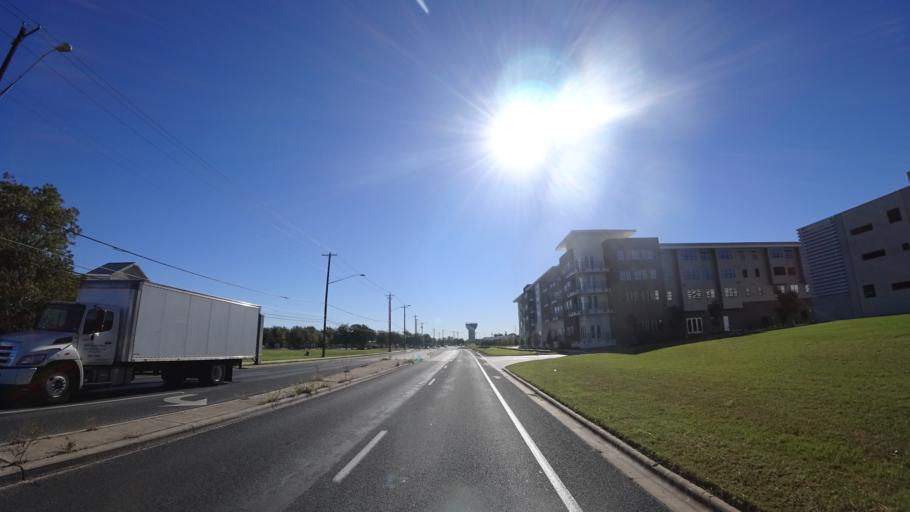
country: US
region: Texas
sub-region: Travis County
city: Austin
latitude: 30.3053
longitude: -97.7021
